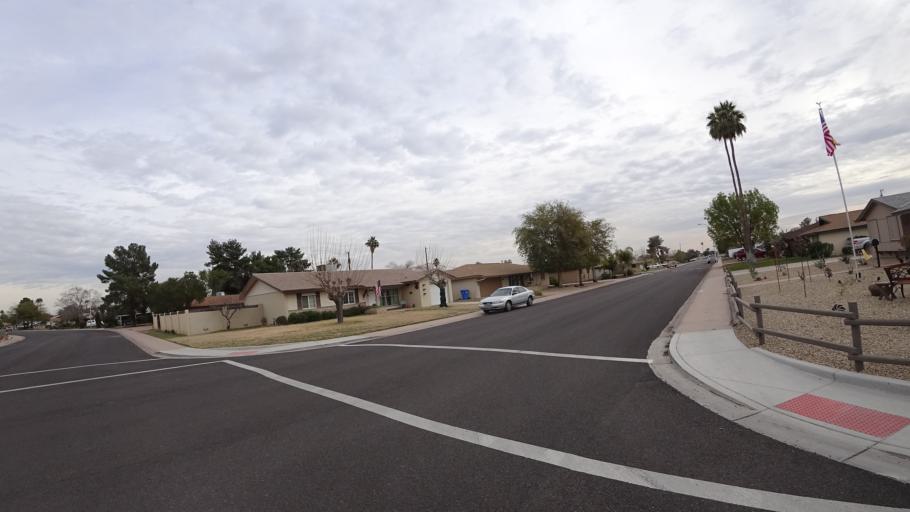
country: US
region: Arizona
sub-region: Maricopa County
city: Glendale
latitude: 33.6140
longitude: -112.1291
